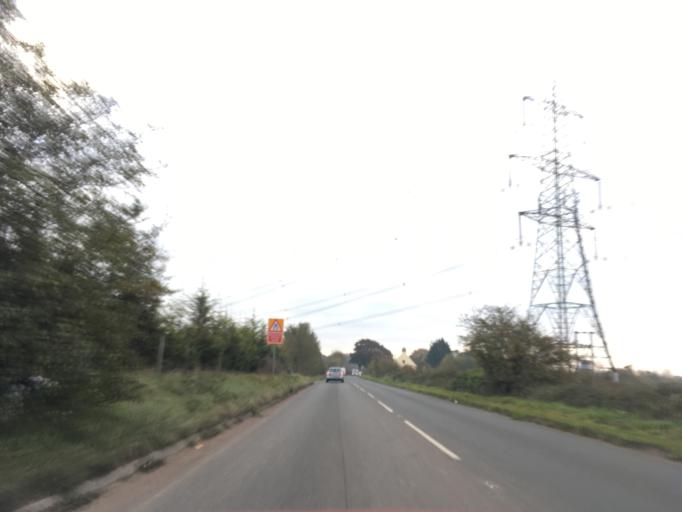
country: GB
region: England
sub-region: South Gloucestershire
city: Yate
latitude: 51.5252
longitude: -2.4354
